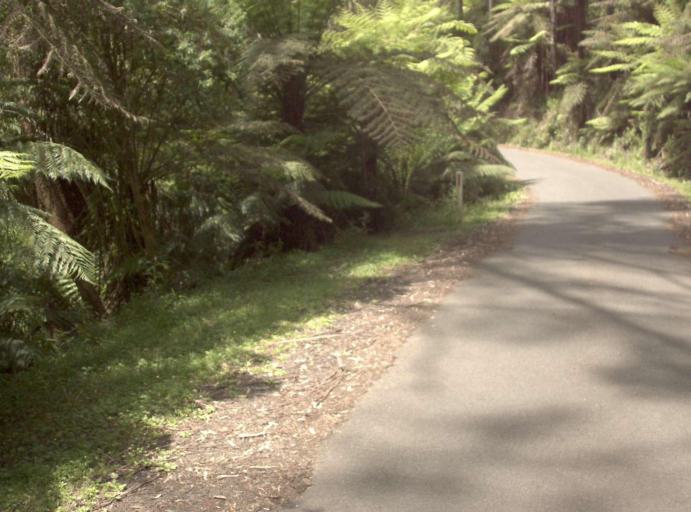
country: AU
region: Victoria
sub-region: Latrobe
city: Traralgon
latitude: -38.4401
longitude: 146.5352
